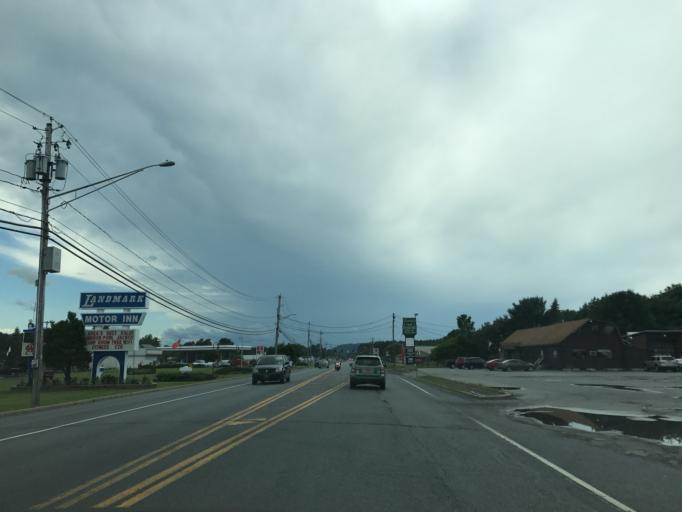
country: US
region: New York
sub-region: Warren County
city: West Glens Falls
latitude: 43.2518
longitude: -73.6683
